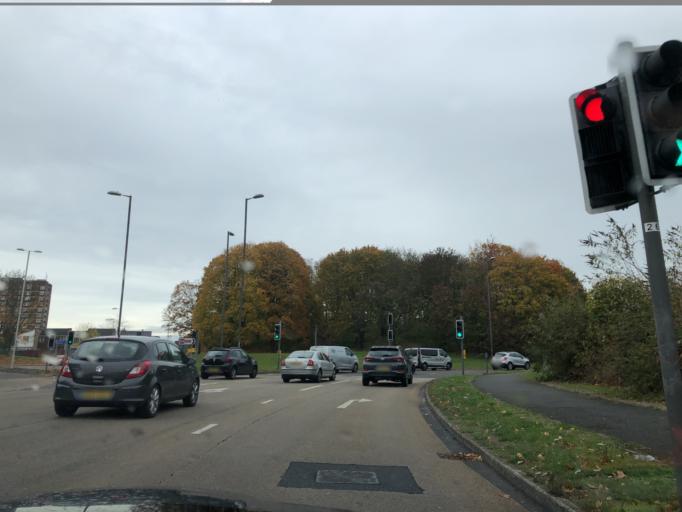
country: GB
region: England
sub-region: Hampshire
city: Basingstoke
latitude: 51.2765
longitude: -1.0758
